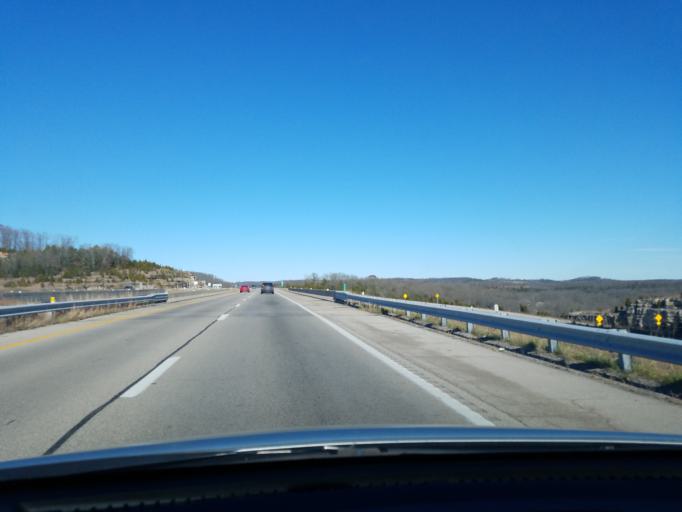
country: US
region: Missouri
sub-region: Taney County
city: Merriam Woods
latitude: 36.7485
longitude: -93.2227
